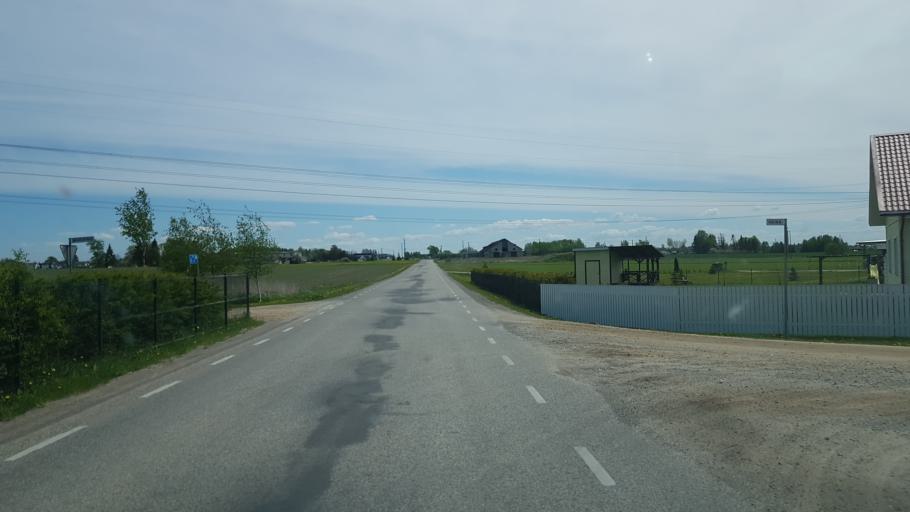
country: EE
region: Tartu
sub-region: Tartu linn
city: Tartu
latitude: 58.3536
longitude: 26.6479
